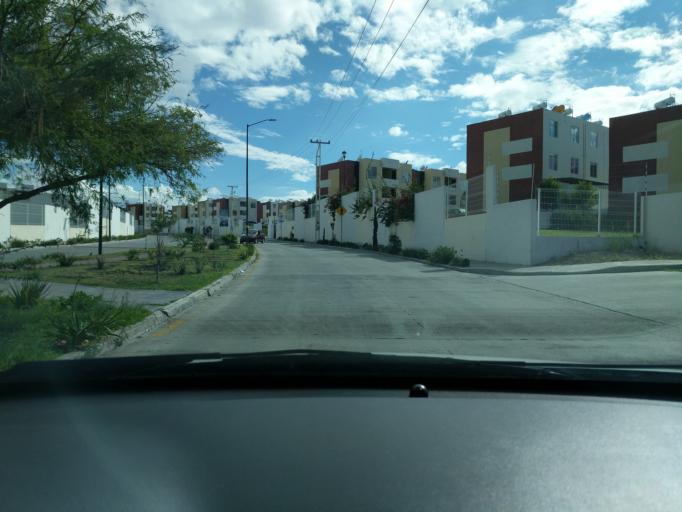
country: MX
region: Queretaro
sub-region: El Marques
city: La Loma
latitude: 20.5883
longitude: -100.2615
